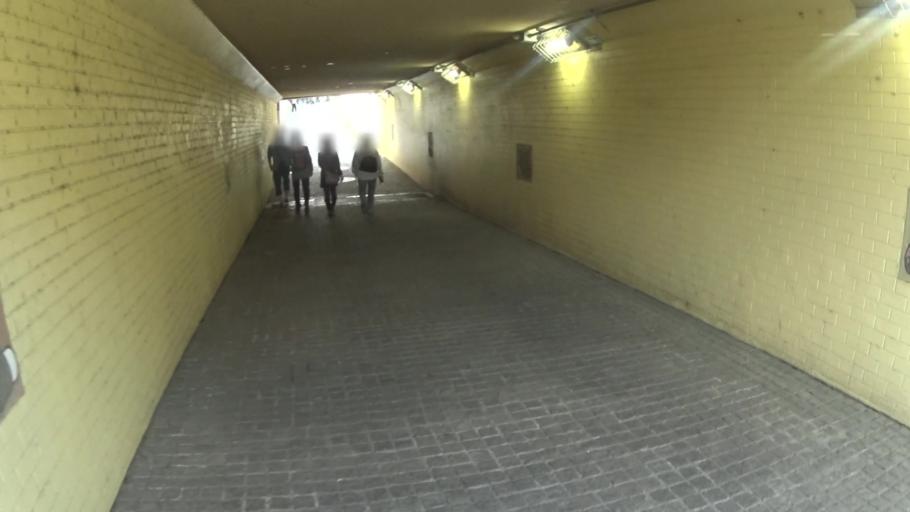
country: JP
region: Tokyo
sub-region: Machida-shi
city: Machida
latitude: 35.5842
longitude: 139.4874
